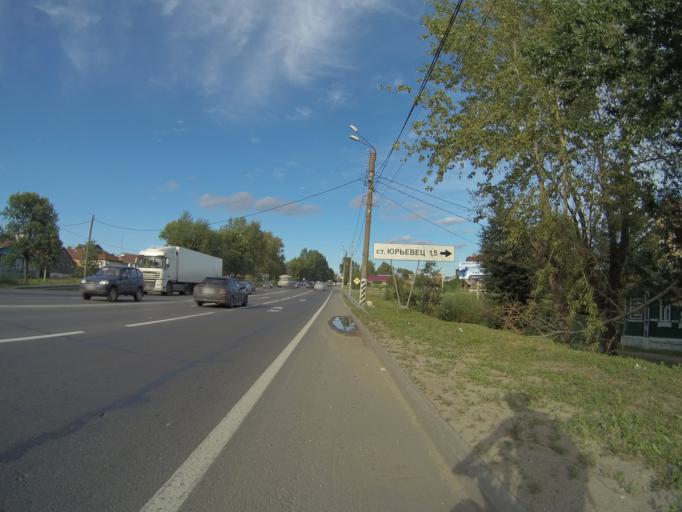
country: RU
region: Vladimir
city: Raduzhnyy
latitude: 56.0978
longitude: 40.2619
